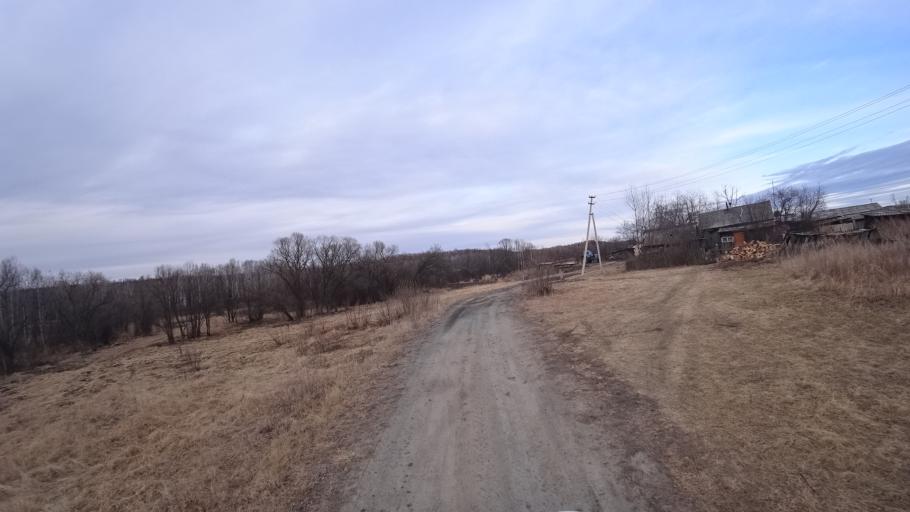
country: RU
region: Amur
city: Bureya
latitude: 50.0219
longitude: 129.7666
